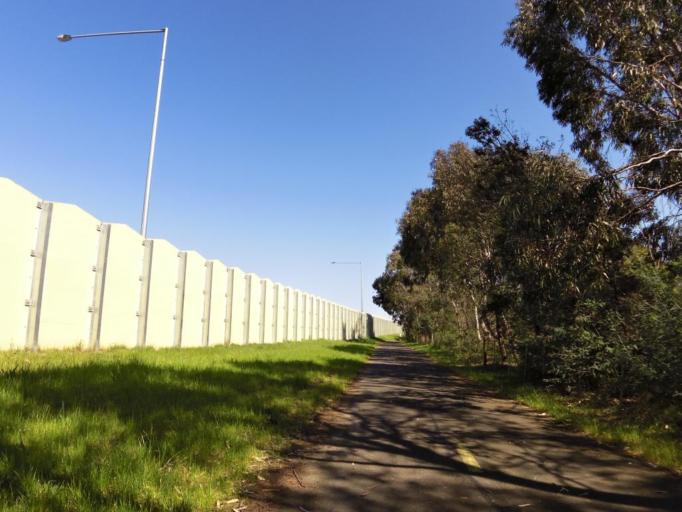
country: AU
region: Victoria
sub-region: Whittlesea
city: Thomastown
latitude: -37.6872
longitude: 145.0389
